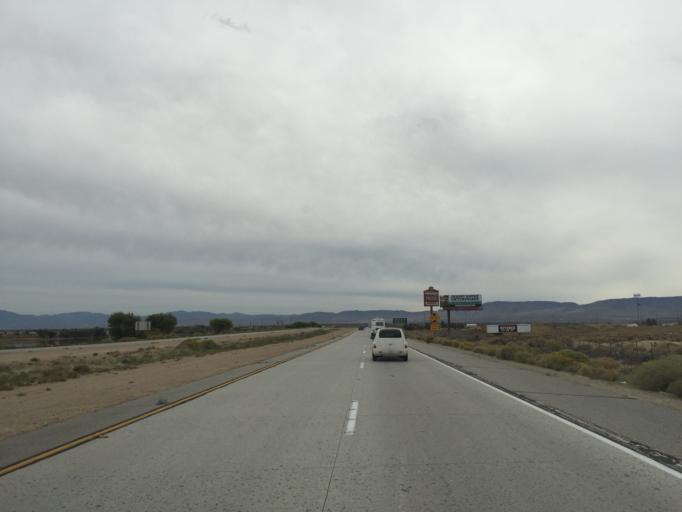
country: US
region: California
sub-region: Los Angeles County
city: Lancaster
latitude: 34.7277
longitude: -118.1705
